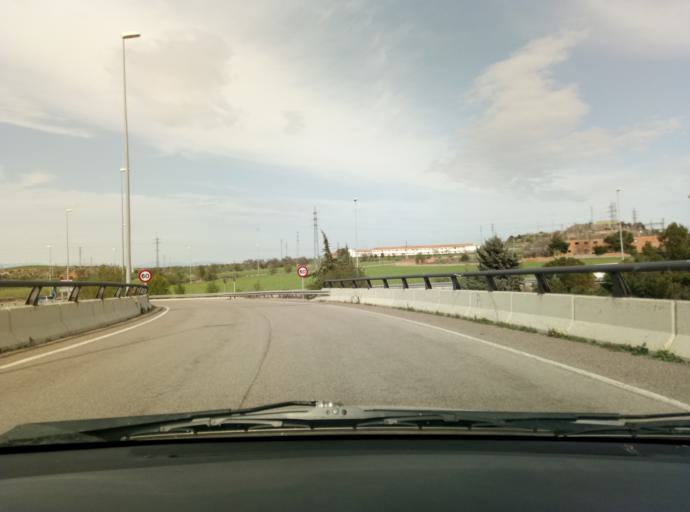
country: ES
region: Catalonia
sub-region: Provincia de Lleida
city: Cervera
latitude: 41.6802
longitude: 1.2860
